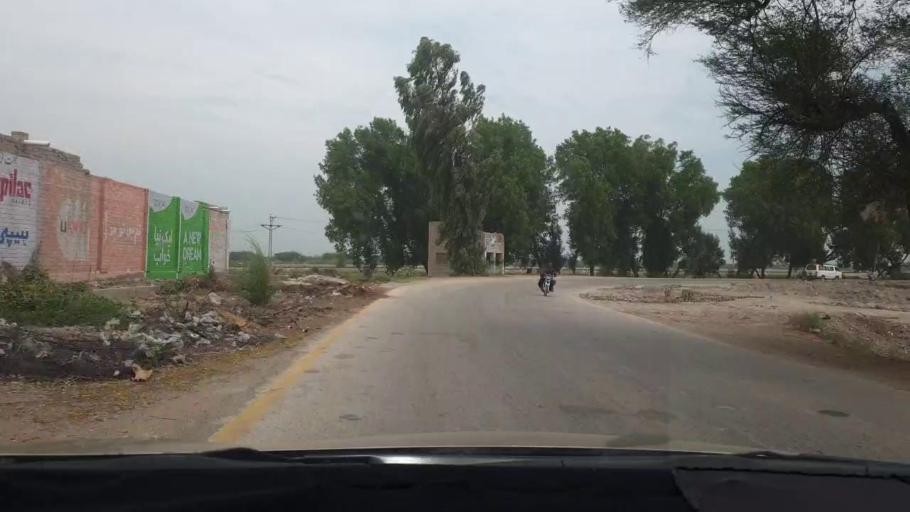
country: PK
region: Sindh
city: Naudero
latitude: 27.6617
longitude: 68.3437
